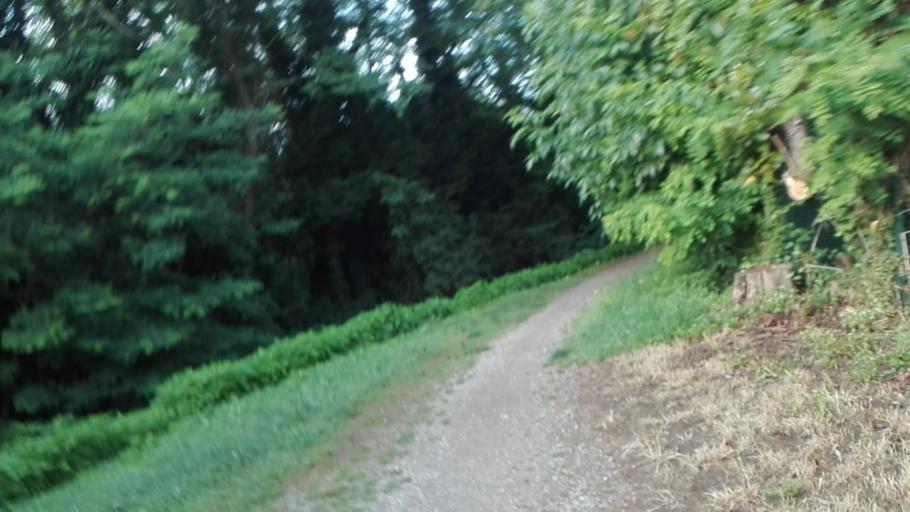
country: IT
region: Emilia-Romagna
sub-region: Provincia di Bologna
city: Bologna
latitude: 44.5272
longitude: 11.3390
